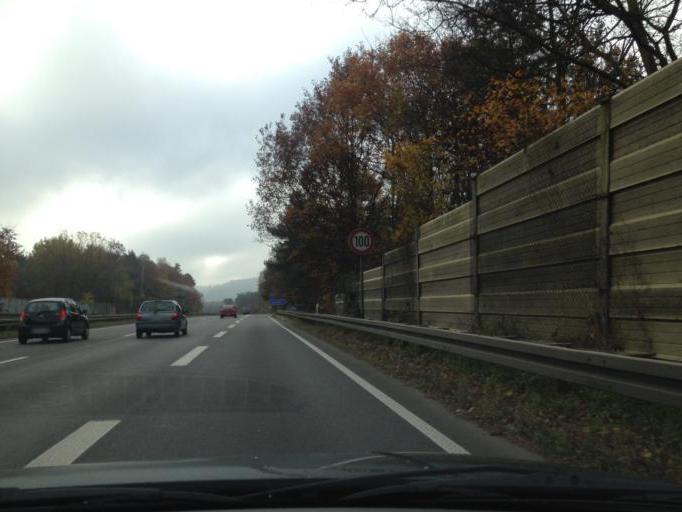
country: DE
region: Saarland
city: Bexbach
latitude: 49.3185
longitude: 7.2387
